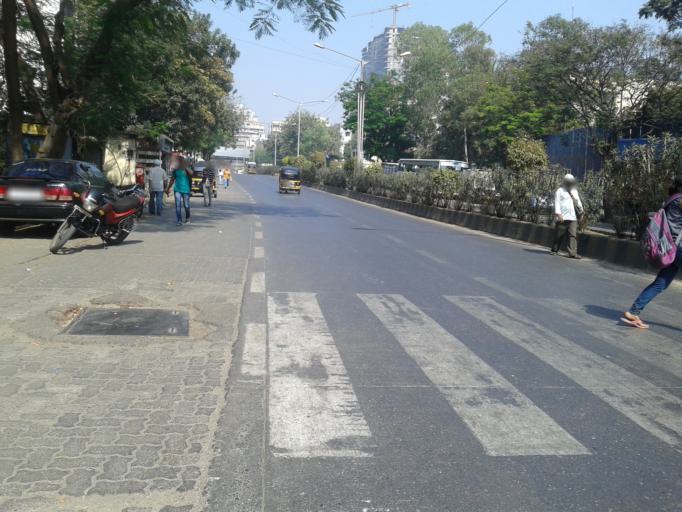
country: IN
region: Maharashtra
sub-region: Mumbai Suburban
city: Borivli
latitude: 19.2473
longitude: 72.8618
